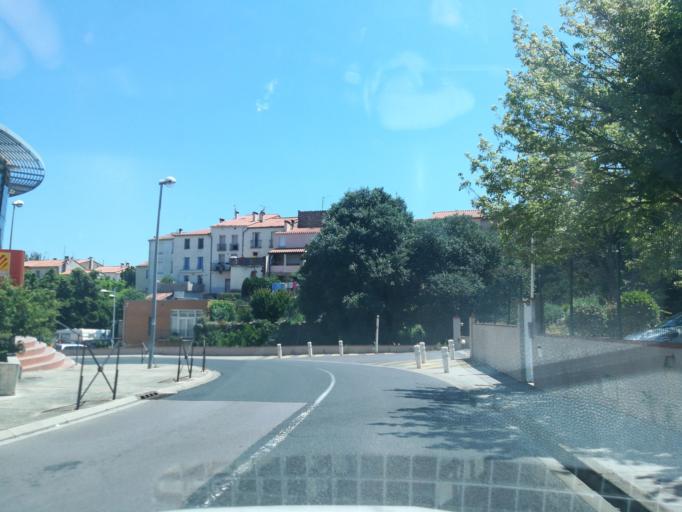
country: FR
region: Languedoc-Roussillon
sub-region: Departement des Pyrenees-Orientales
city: Ceret
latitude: 42.4882
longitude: 2.7460
